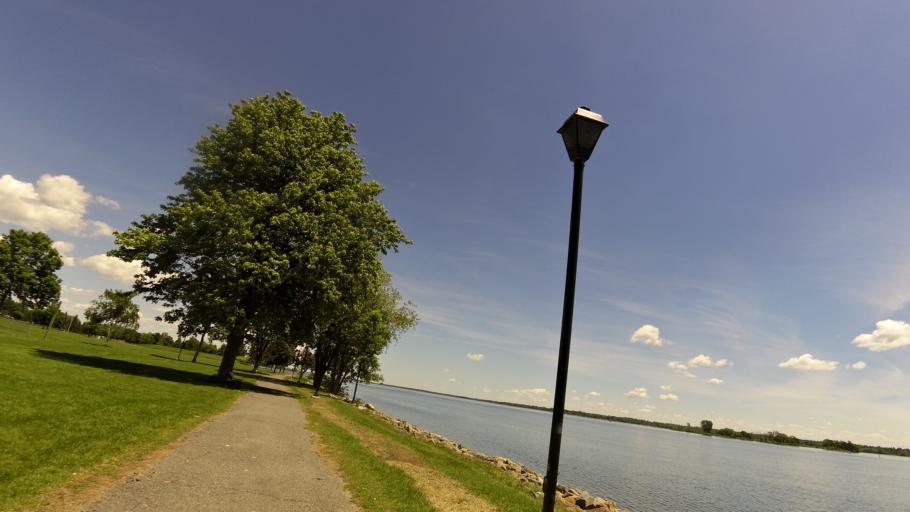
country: US
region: New York
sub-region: St. Lawrence County
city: Norfolk
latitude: 44.8950
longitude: -75.1784
